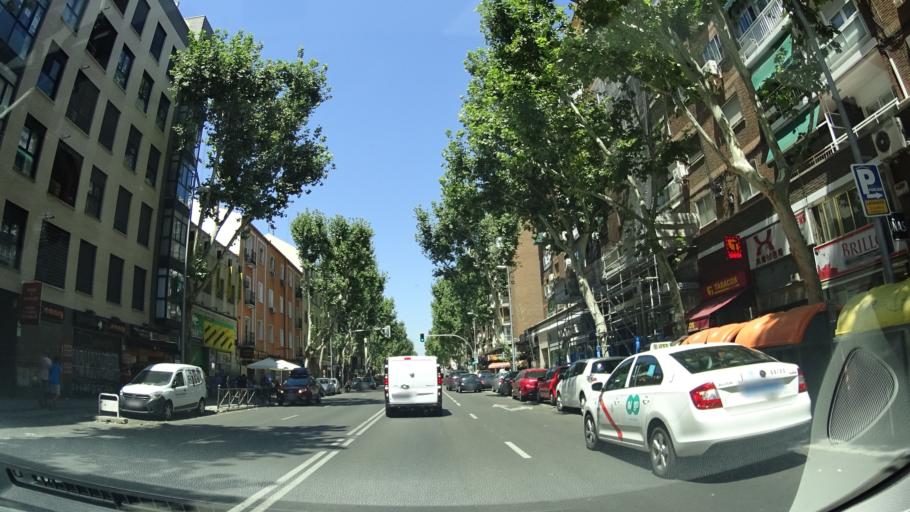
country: ES
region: Madrid
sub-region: Provincia de Madrid
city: Usera
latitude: 40.3946
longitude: -3.7091
